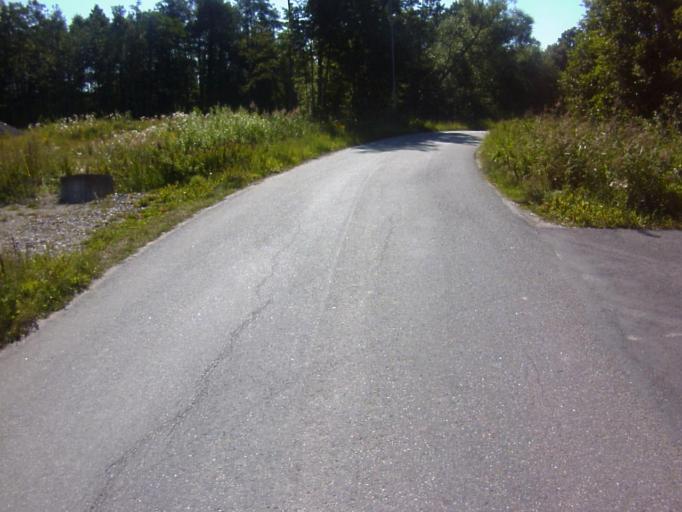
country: SE
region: Soedermanland
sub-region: Eskilstuna Kommun
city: Torshalla
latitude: 59.3868
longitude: 16.4794
